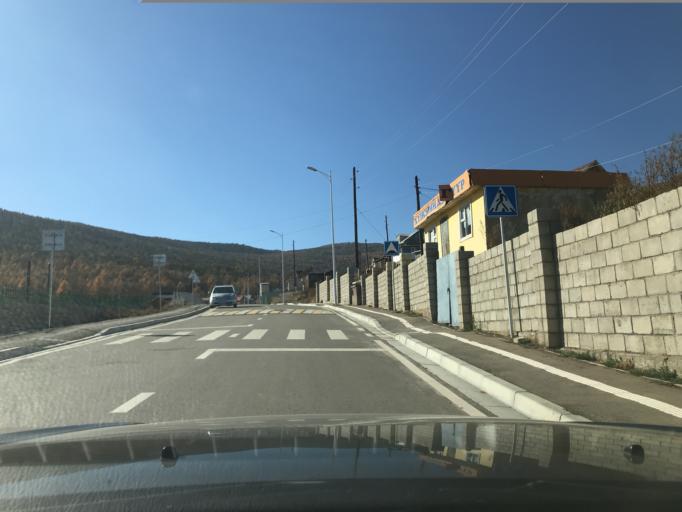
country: MN
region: Ulaanbaatar
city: Ulaanbaatar
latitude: 48.0389
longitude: 106.8954
